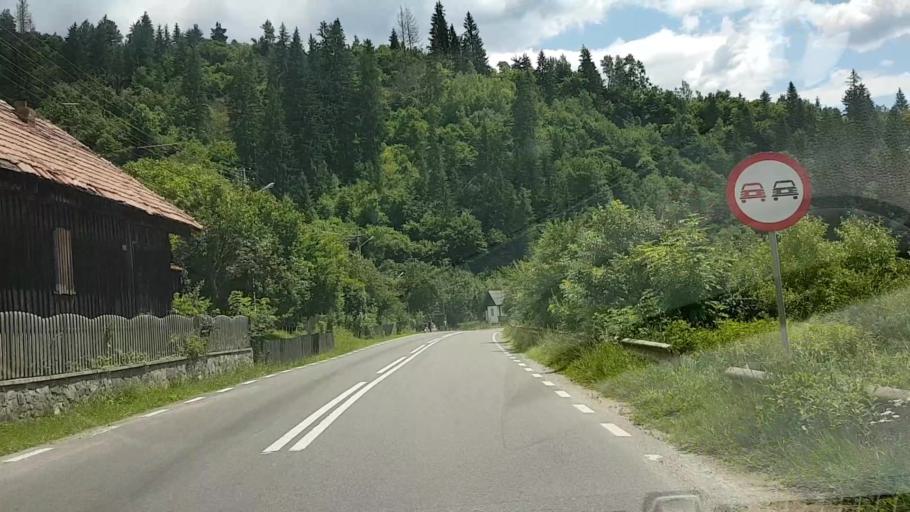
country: RO
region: Suceava
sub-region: Comuna Brosteni
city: Brosteni
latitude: 47.2542
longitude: 25.6947
